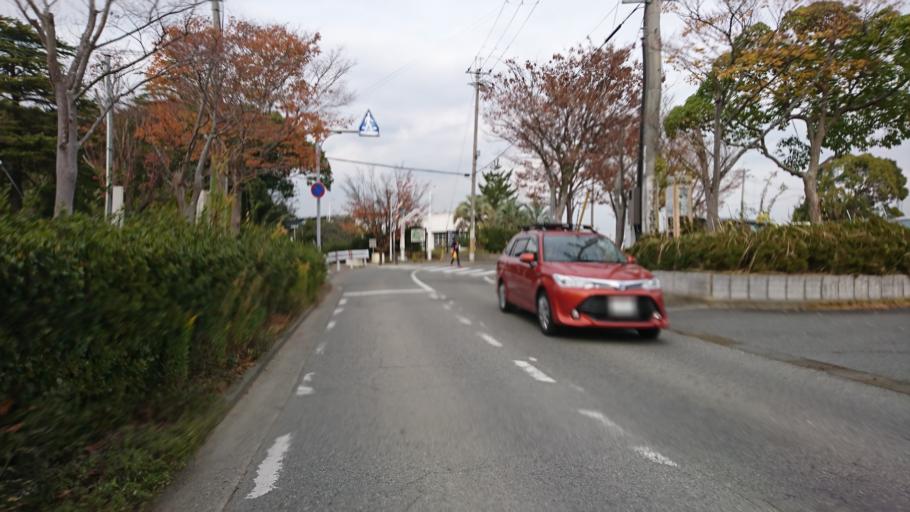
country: JP
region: Hyogo
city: Kakogawacho-honmachi
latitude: 34.7756
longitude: 134.8651
